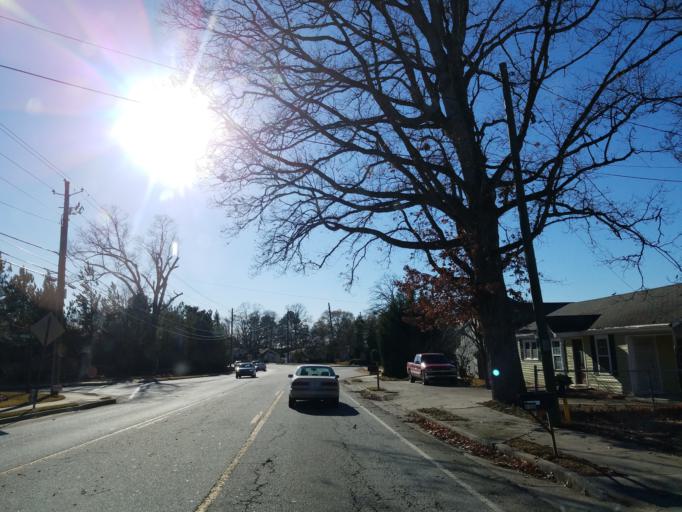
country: US
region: Georgia
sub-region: Cobb County
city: Mableton
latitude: 33.8033
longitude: -84.5118
